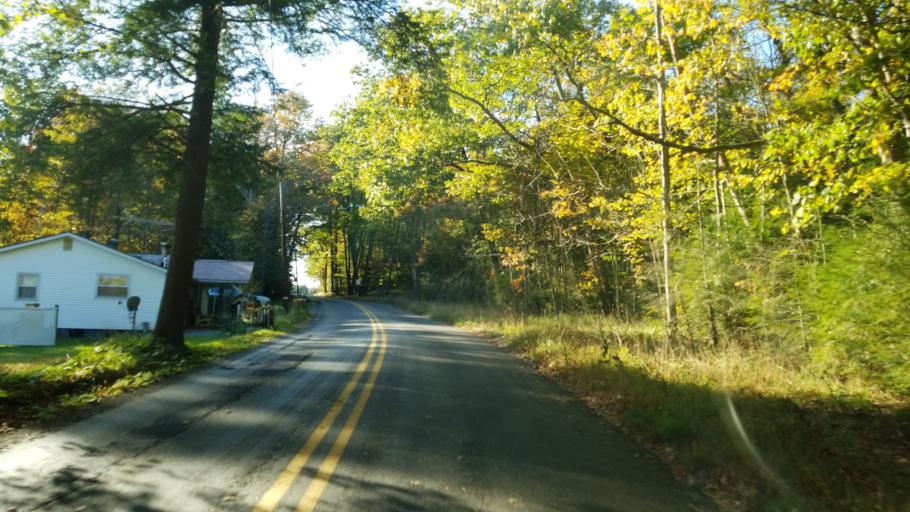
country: US
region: Pennsylvania
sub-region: Indiana County
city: Johnsonburg
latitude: 40.8958
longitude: -78.8824
